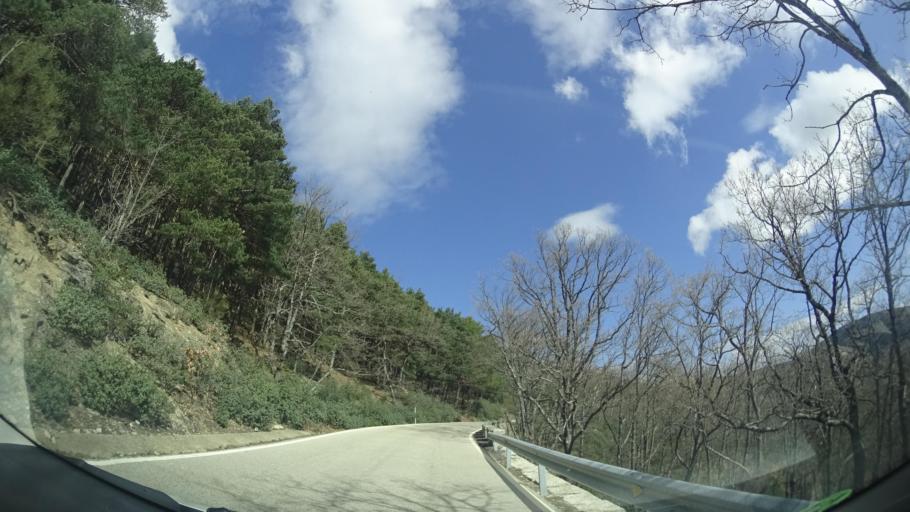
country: ES
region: Madrid
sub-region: Provincia de Madrid
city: Miraflores de la Sierra
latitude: 40.8507
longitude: -3.7660
